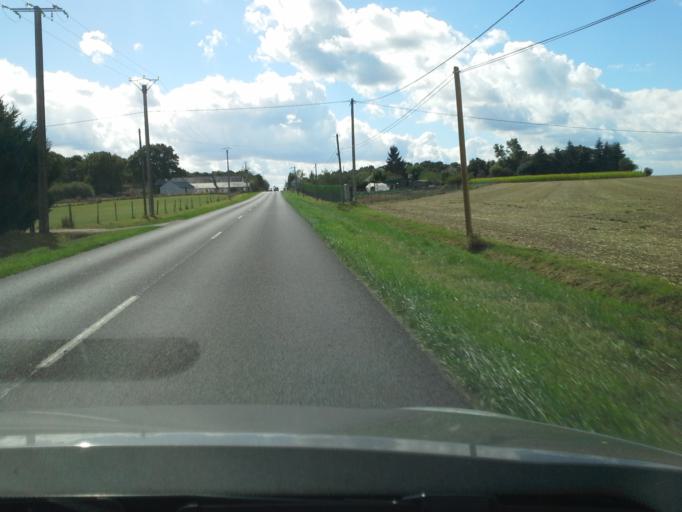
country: FR
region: Centre
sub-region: Departement du Loir-et-Cher
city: Pontlevoy
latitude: 47.4188
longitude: 1.2781
